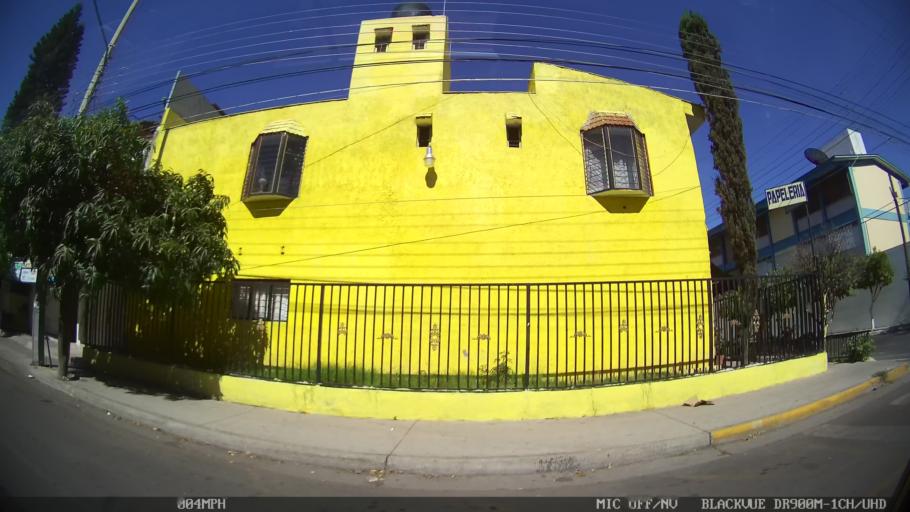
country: MX
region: Jalisco
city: Tlaquepaque
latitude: 20.6604
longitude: -103.2897
